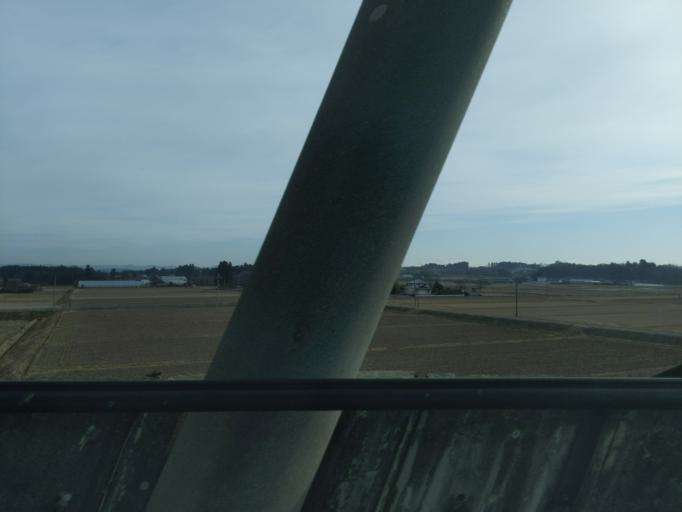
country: JP
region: Iwate
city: Ichinoseki
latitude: 38.7524
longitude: 141.0737
